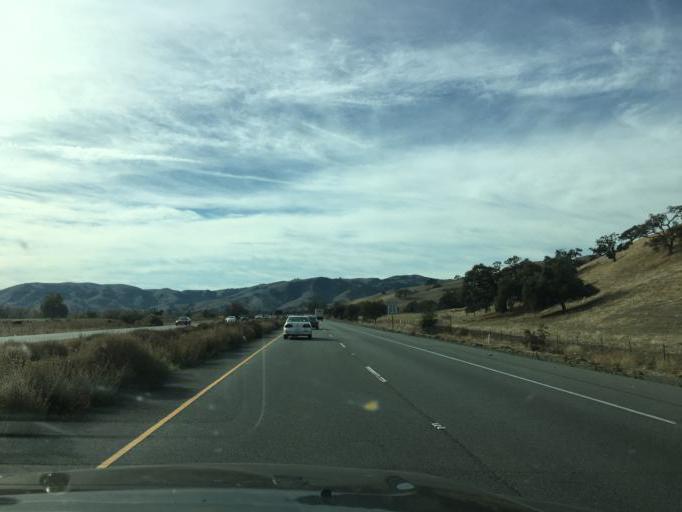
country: US
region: California
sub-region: San Benito County
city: Hollister
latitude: 37.0118
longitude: -121.3507
